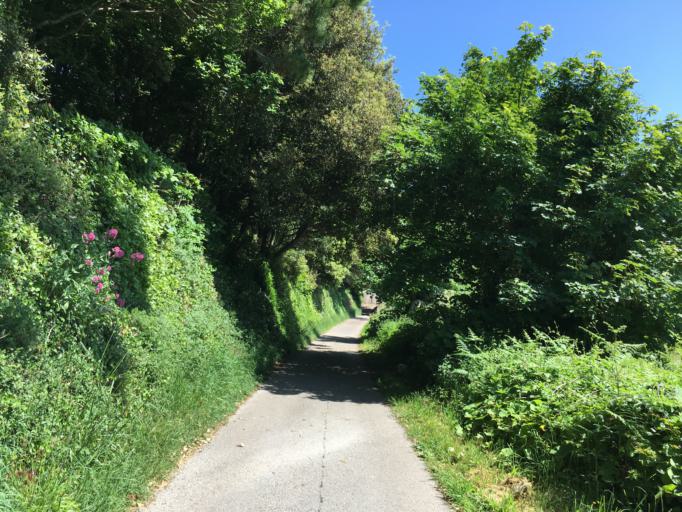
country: GB
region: England
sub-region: Devon
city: Dartmouth
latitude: 50.3458
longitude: -3.5552
